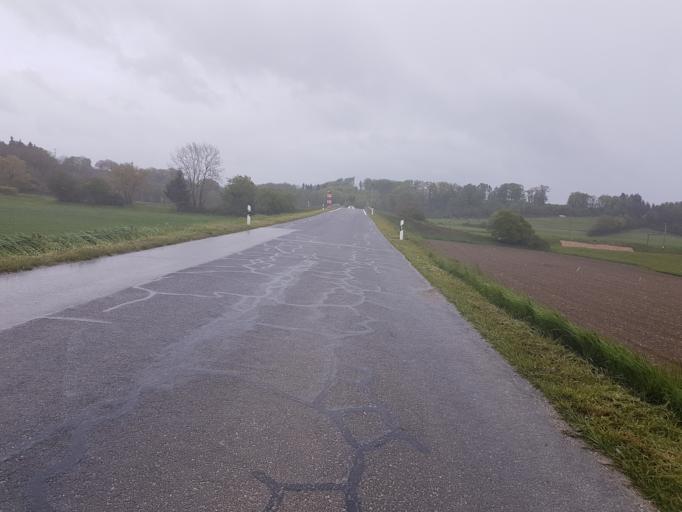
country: CH
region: Vaud
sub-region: Gros-de-Vaud District
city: Penthalaz
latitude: 46.6255
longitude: 6.5267
